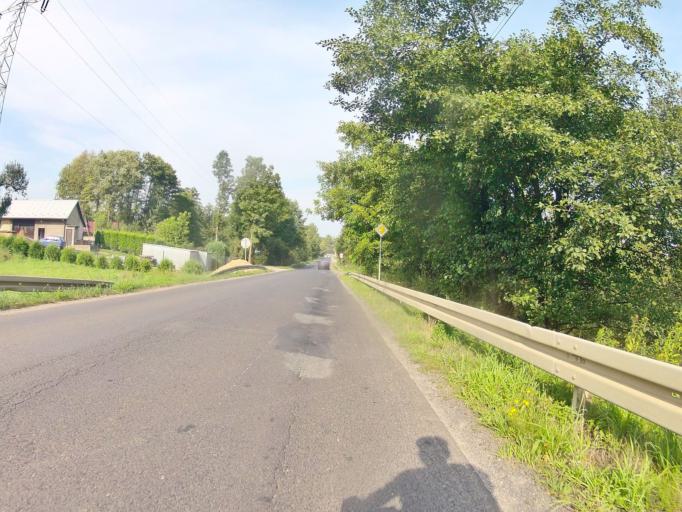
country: PL
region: Subcarpathian Voivodeship
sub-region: Powiat jasielski
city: Trzcinica
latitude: 49.7620
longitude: 21.4327
